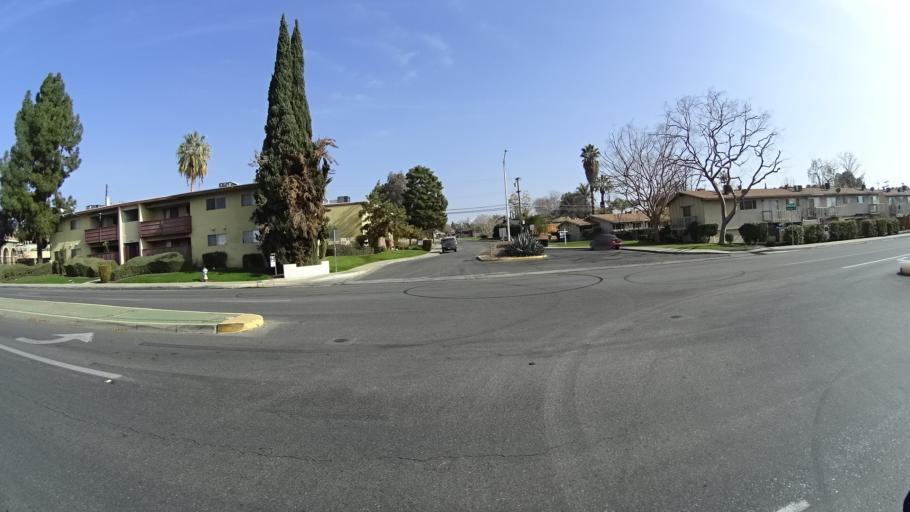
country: US
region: California
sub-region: Kern County
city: Oildale
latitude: 35.3991
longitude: -118.9500
